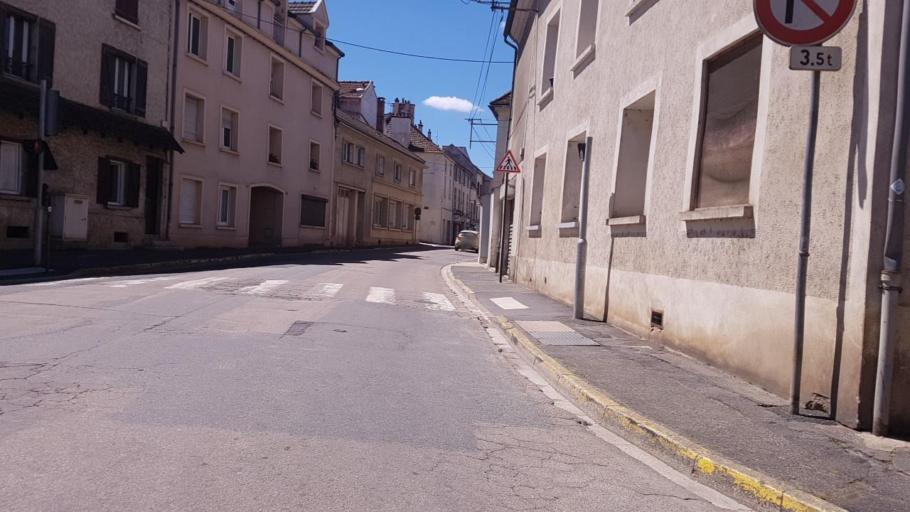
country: FR
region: Ile-de-France
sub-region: Departement de Seine-et-Marne
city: La Ferte-sous-Jouarre
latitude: 48.9483
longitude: 3.1337
